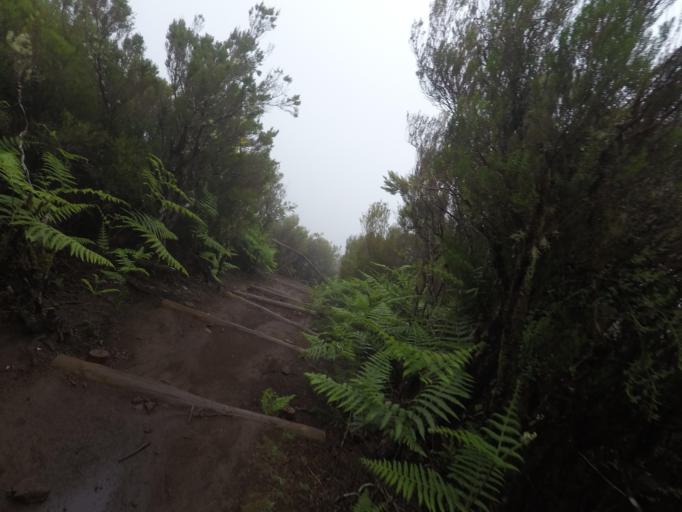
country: PT
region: Madeira
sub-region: Calheta
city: Arco da Calheta
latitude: 32.7685
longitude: -17.1169
